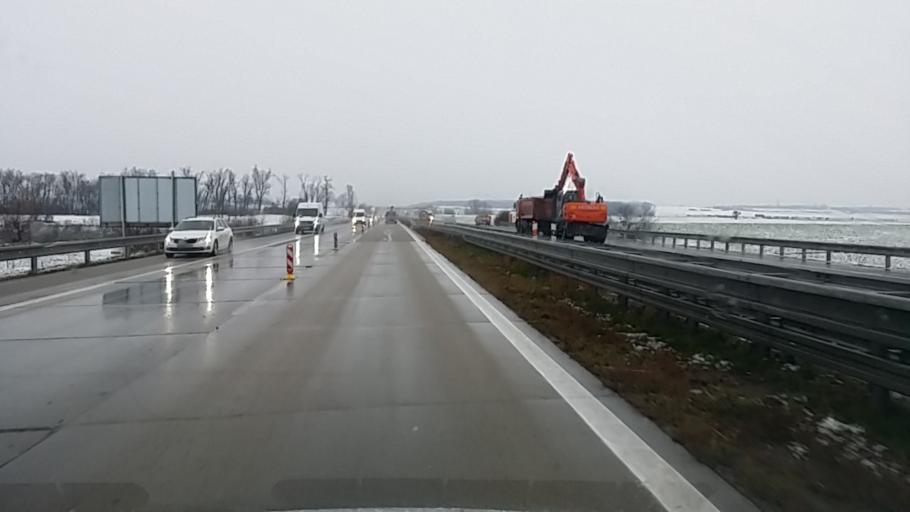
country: CZ
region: South Moravian
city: Rajhradice
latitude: 49.0904
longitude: 16.6569
